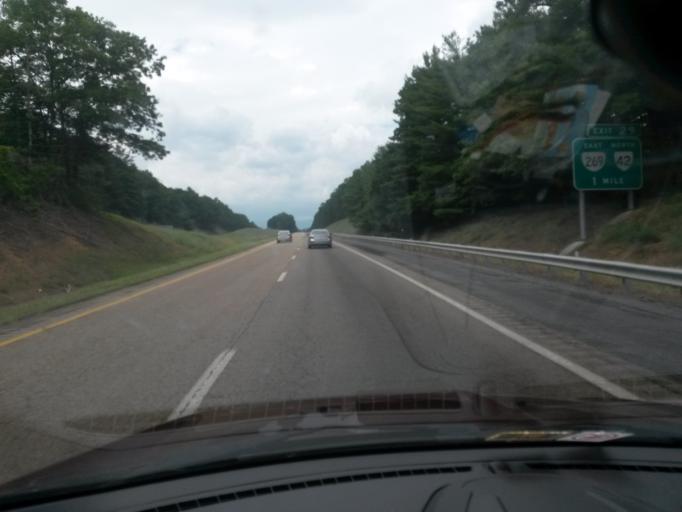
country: US
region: Virginia
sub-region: Alleghany County
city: Clifton Forge
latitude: 37.8214
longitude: -79.7440
